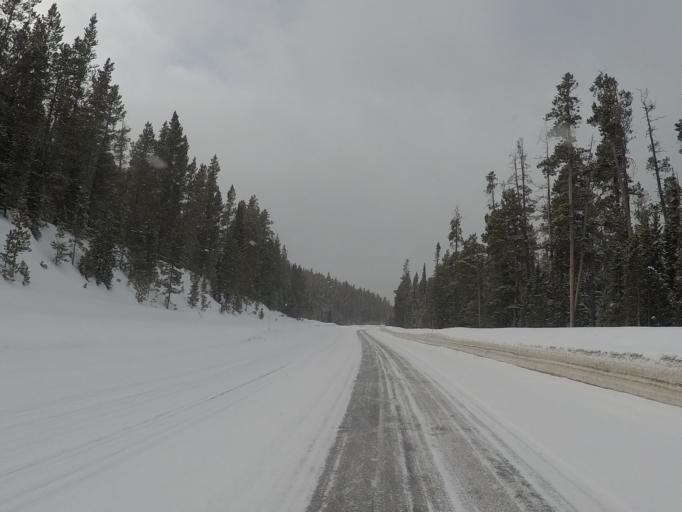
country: US
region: Montana
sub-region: Meagher County
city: White Sulphur Springs
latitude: 46.8490
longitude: -110.6895
